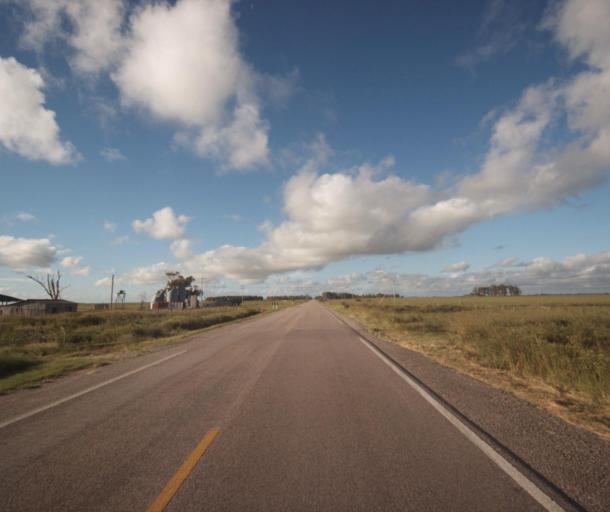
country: BR
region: Rio Grande do Sul
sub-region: Arroio Grande
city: Arroio Grande
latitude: -32.3811
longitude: -52.5533
